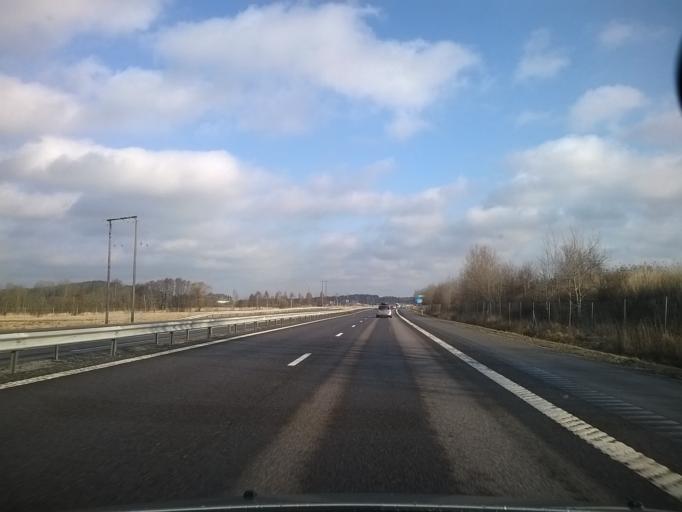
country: SE
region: Vaestra Goetaland
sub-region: Stenungsunds Kommun
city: Stora Hoga
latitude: 58.0131
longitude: 11.8434
